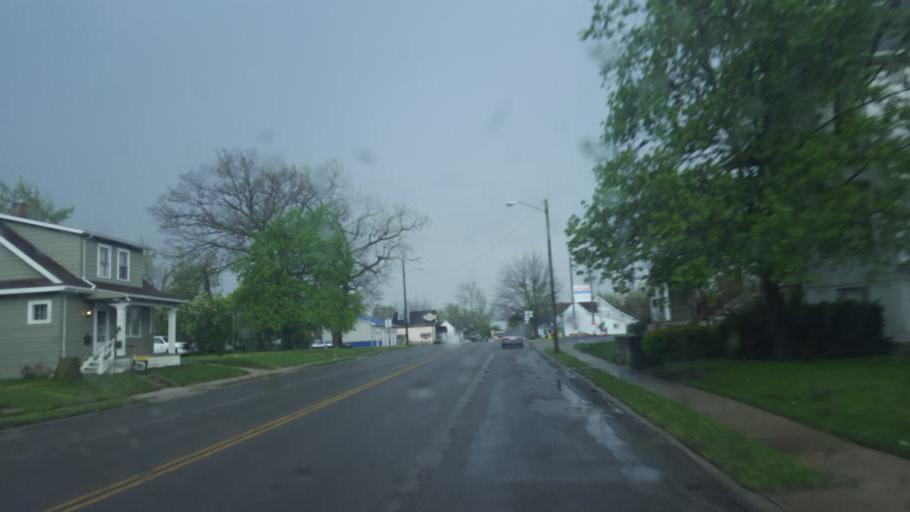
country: US
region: Ohio
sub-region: Seneca County
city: Fostoria
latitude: 41.1575
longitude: -83.4212
